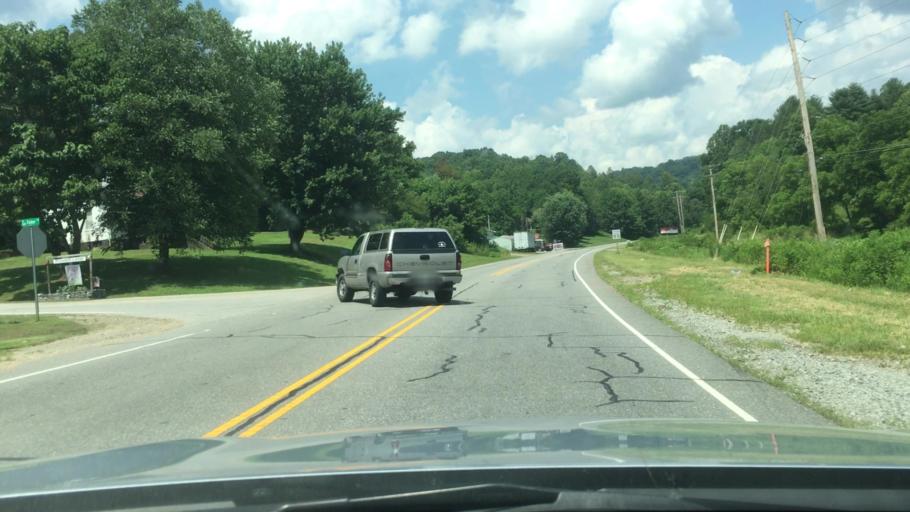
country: US
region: North Carolina
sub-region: Madison County
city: Marshall
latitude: 35.8154
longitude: -82.6542
